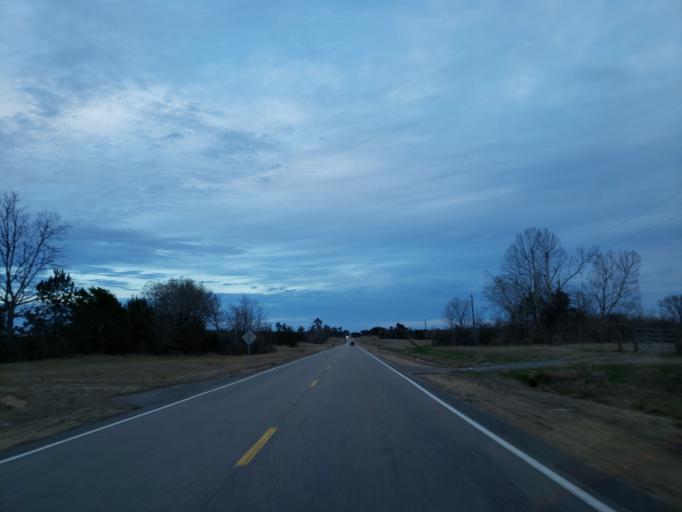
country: US
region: Mississippi
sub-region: Kemper County
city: De Kalb
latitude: 32.8308
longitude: -88.3790
